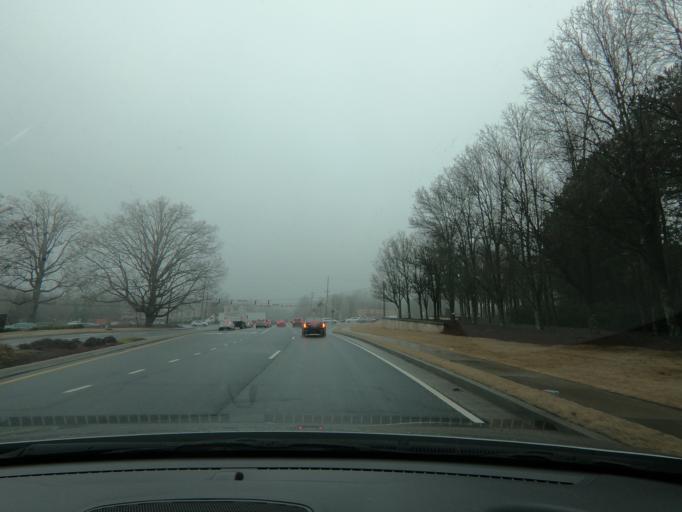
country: US
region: Georgia
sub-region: Fulton County
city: Alpharetta
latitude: 34.0687
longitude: -84.2610
